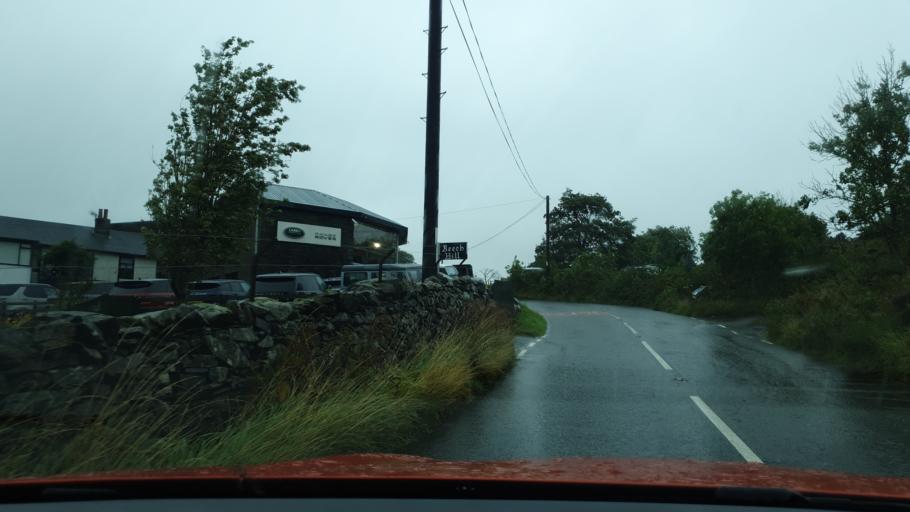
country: GB
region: England
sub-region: Cumbria
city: Ulverston
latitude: 54.3287
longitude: -3.0978
